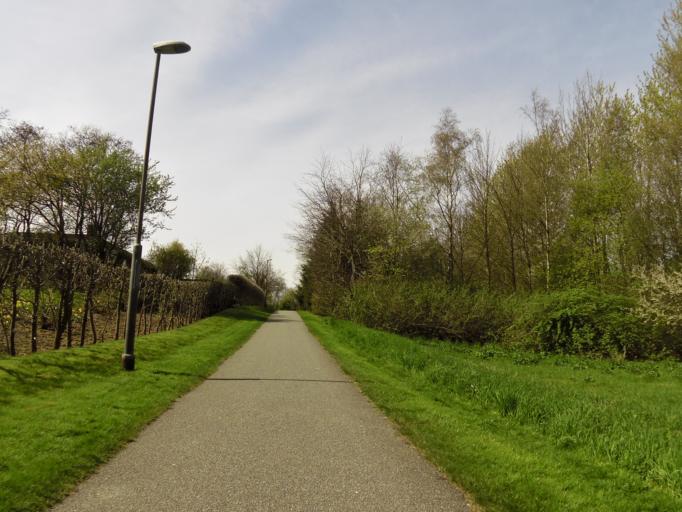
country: DK
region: Central Jutland
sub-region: Skive Kommune
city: Skive
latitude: 56.5846
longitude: 9.0204
